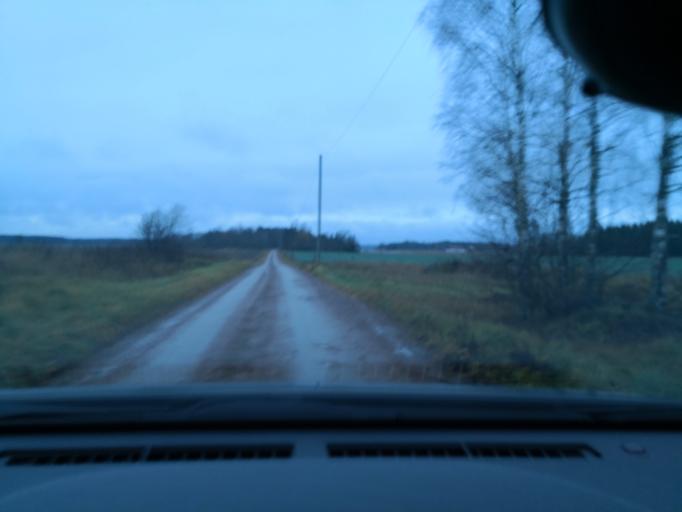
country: SE
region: Vaestmanland
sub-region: Hallstahammars Kommun
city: Kolback
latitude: 59.5584
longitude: 16.1861
